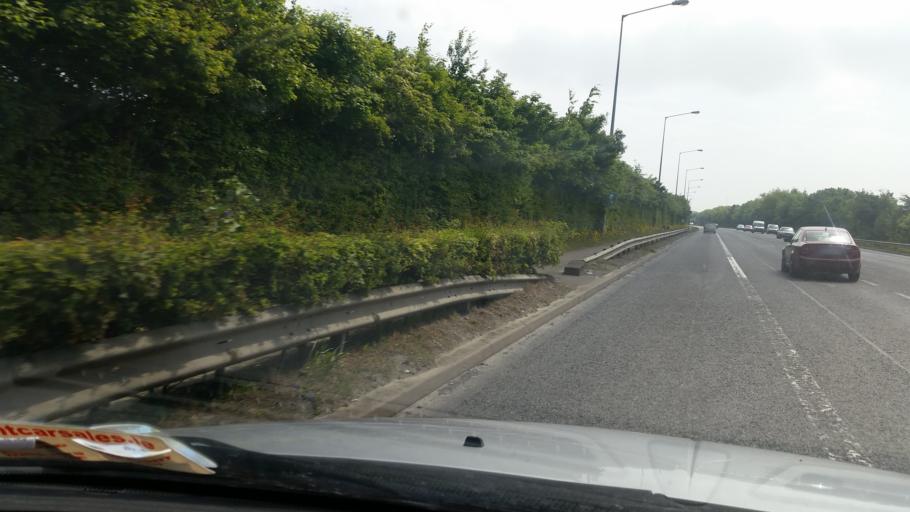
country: IE
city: Darndale
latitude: 53.4063
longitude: -6.1969
